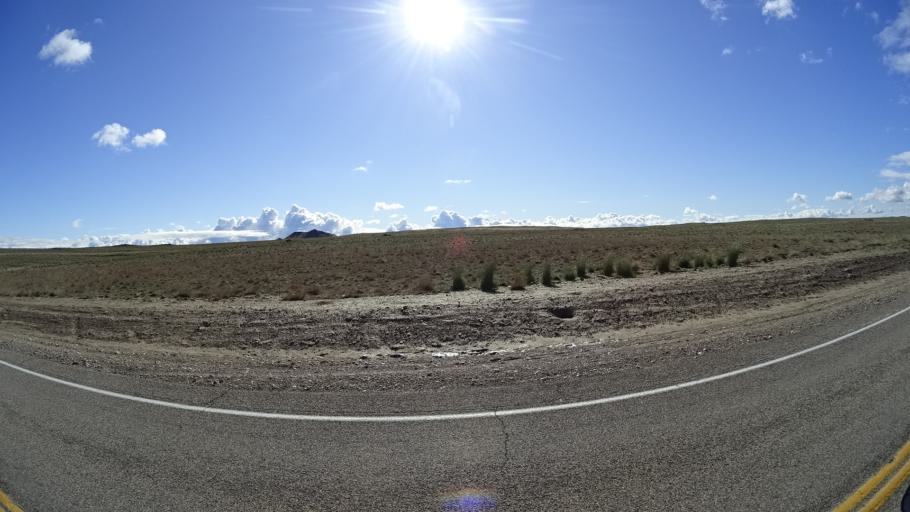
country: US
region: Idaho
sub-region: Ada County
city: Kuna
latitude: 43.3679
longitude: -116.4140
